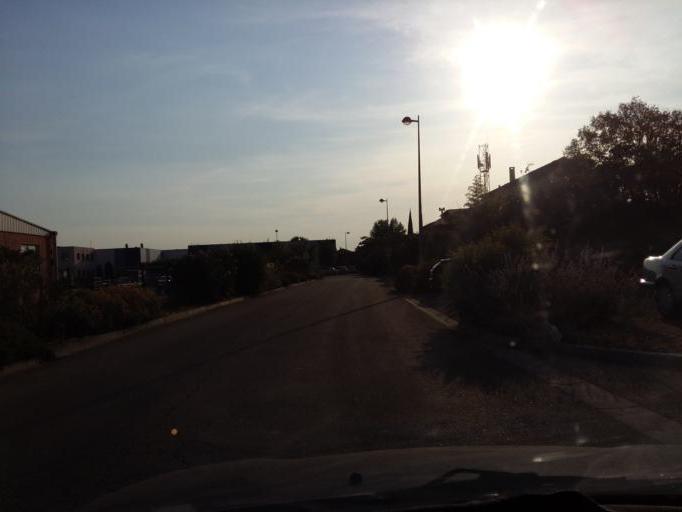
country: FR
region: Provence-Alpes-Cote d'Azur
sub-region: Departement du Vaucluse
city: Monteux
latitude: 44.0316
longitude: 4.9758
